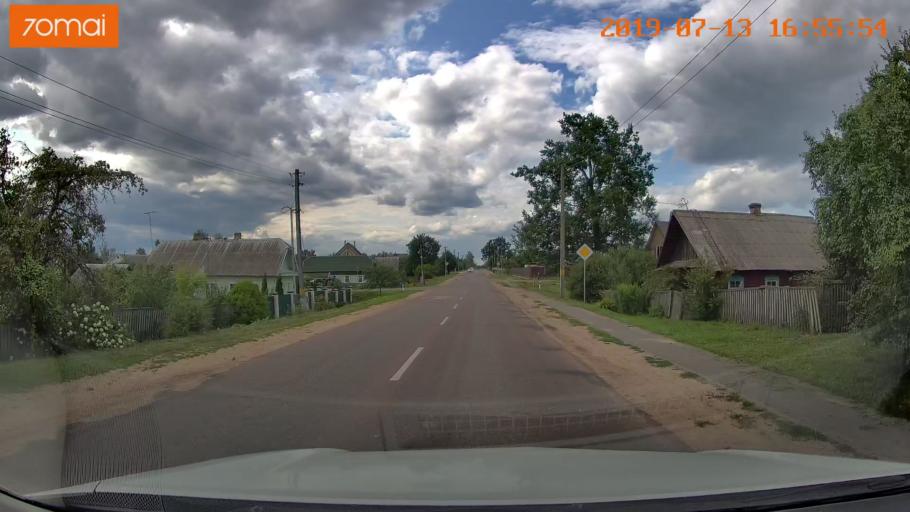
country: BY
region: Mogilev
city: Kirawsk
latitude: 53.2701
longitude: 29.4630
